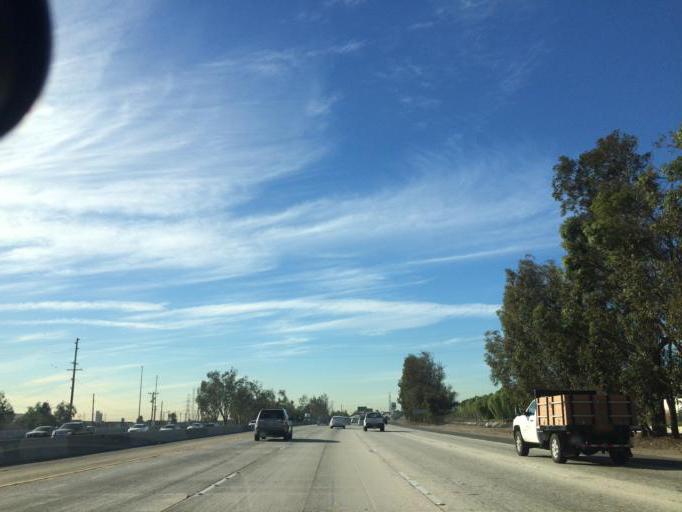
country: US
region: California
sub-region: Riverside County
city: Glen Avon
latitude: 34.0659
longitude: -117.5053
